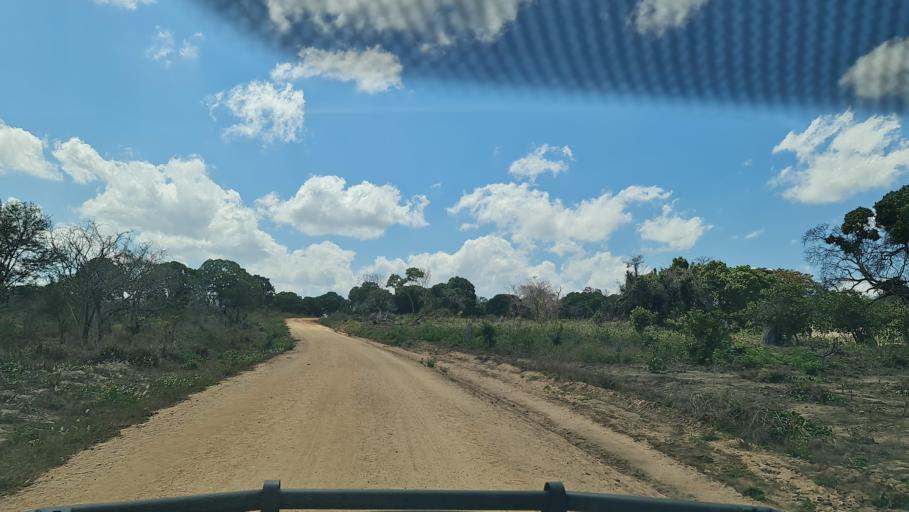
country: MZ
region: Nampula
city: Nacala
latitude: -14.1691
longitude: 40.2548
